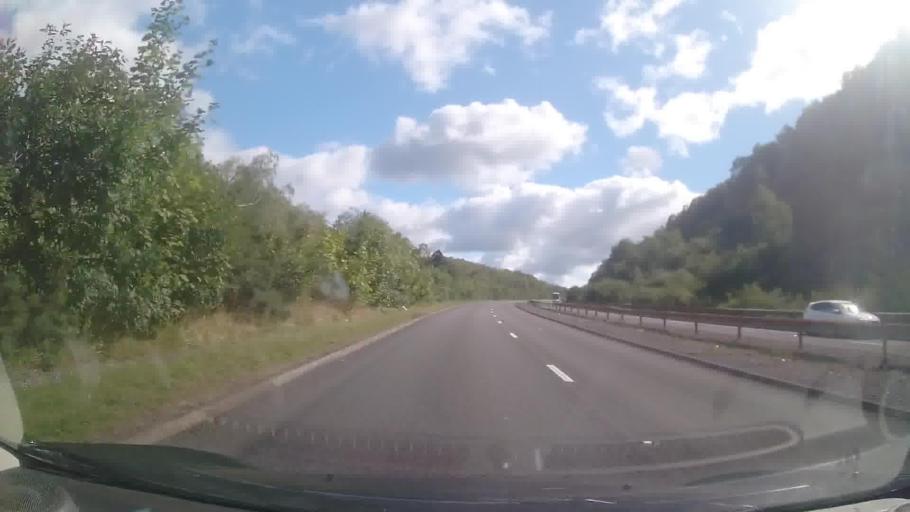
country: GB
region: Wales
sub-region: Neath Port Talbot
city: Glyn-neath
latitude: 51.7573
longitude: -3.5755
